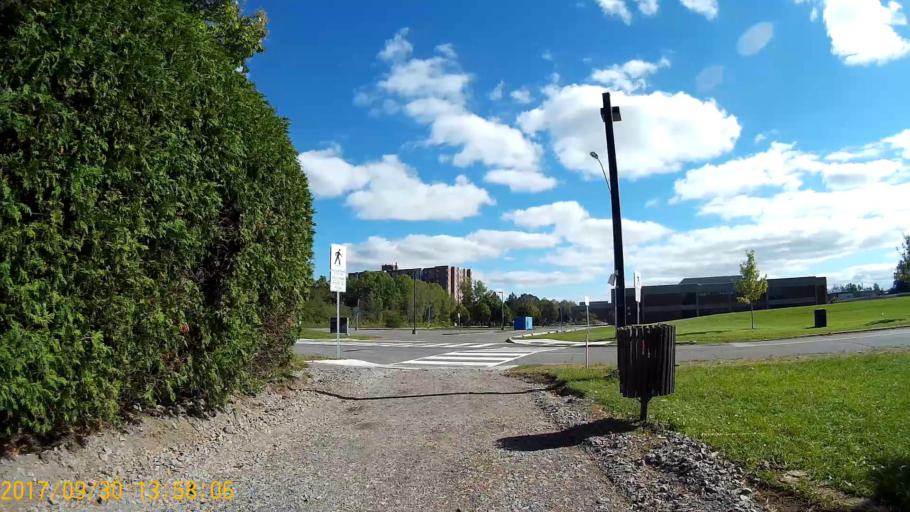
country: CA
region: Ontario
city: Bells Corners
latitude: 45.3239
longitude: -75.8960
